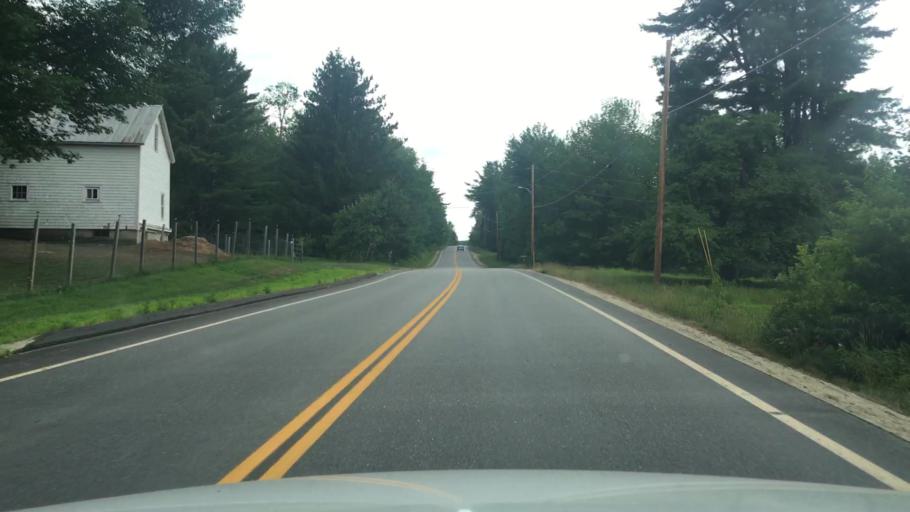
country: US
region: Maine
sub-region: Oxford County
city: Hartford
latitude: 44.3778
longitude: -70.4258
